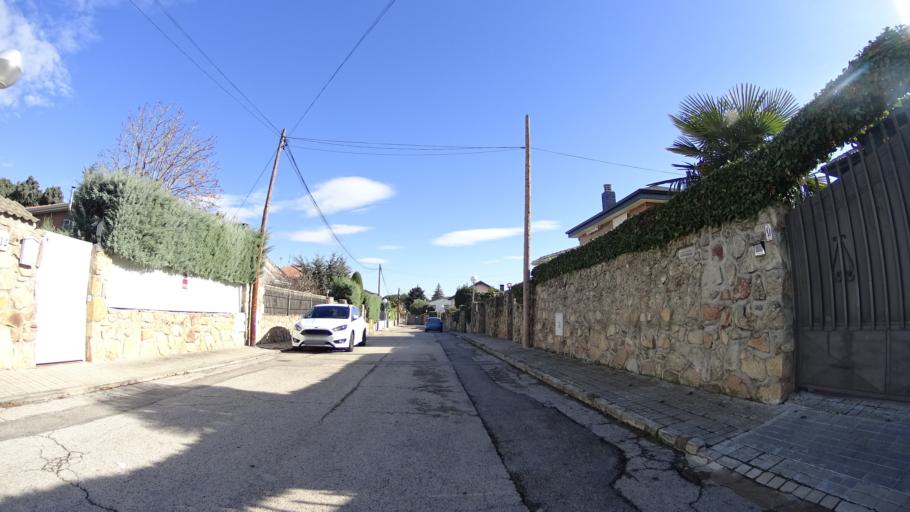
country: ES
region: Madrid
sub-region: Provincia de Madrid
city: Galapagar
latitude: 40.5799
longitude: -4.0206
